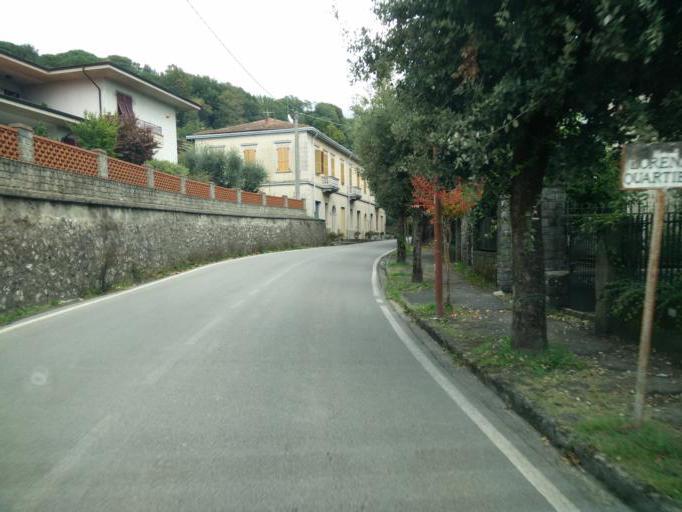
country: IT
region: Tuscany
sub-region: Provincia di Massa-Carrara
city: Bagnone
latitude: 44.3130
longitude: 9.9889
